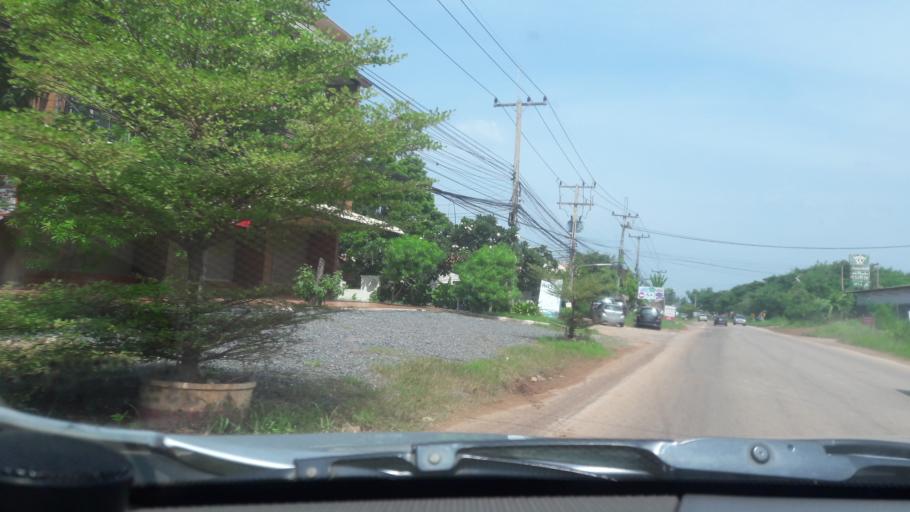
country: TH
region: Changwat Udon Thani
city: Udon Thani
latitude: 17.4336
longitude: 102.8302
